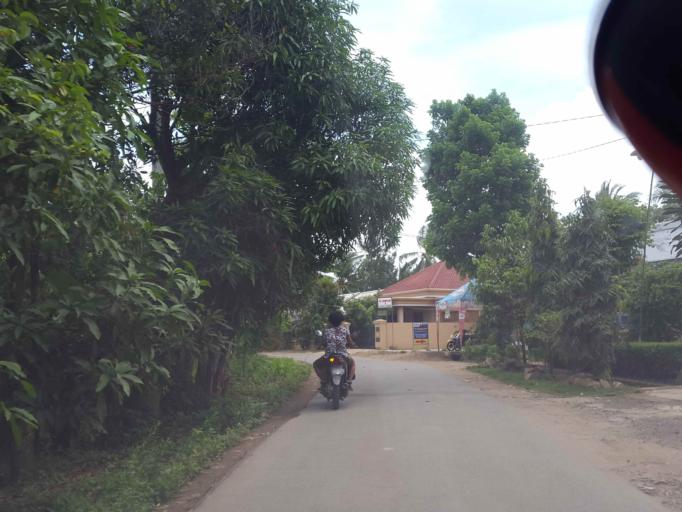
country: ID
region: Lampung
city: Natar
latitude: -5.3144
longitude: 105.2065
